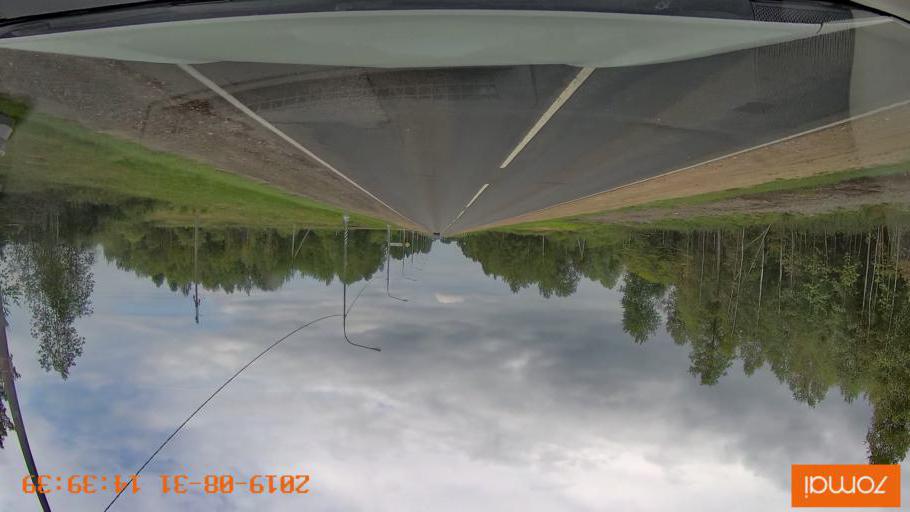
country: RU
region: Smolensk
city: Yekimovichi
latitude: 54.1930
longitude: 33.5573
